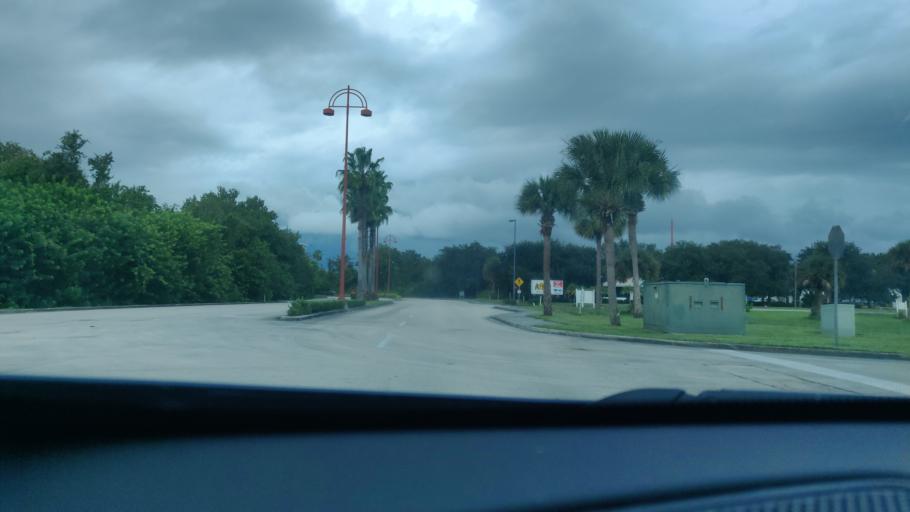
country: US
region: Florida
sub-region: Indian River County
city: West Vero Corridor
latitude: 27.6370
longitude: -80.5223
